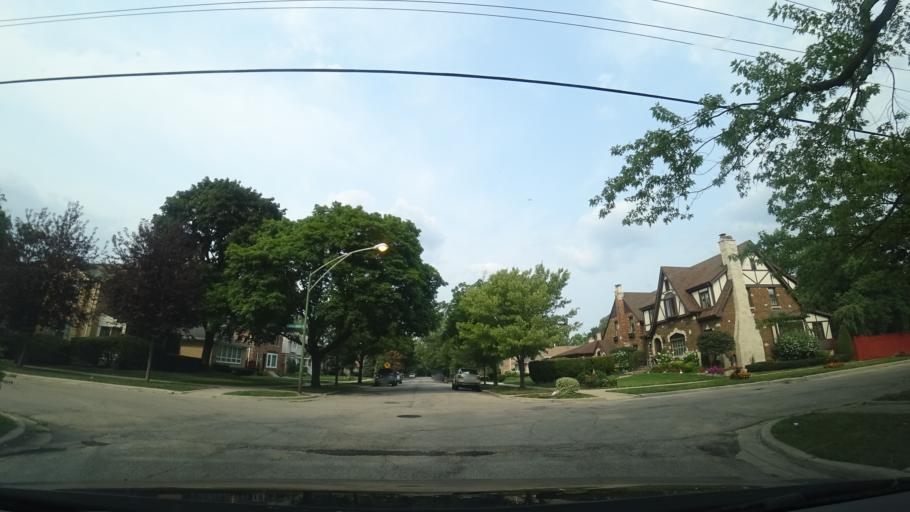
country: US
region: Illinois
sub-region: Cook County
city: Lincolnwood
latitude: 41.9932
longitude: -87.7398
